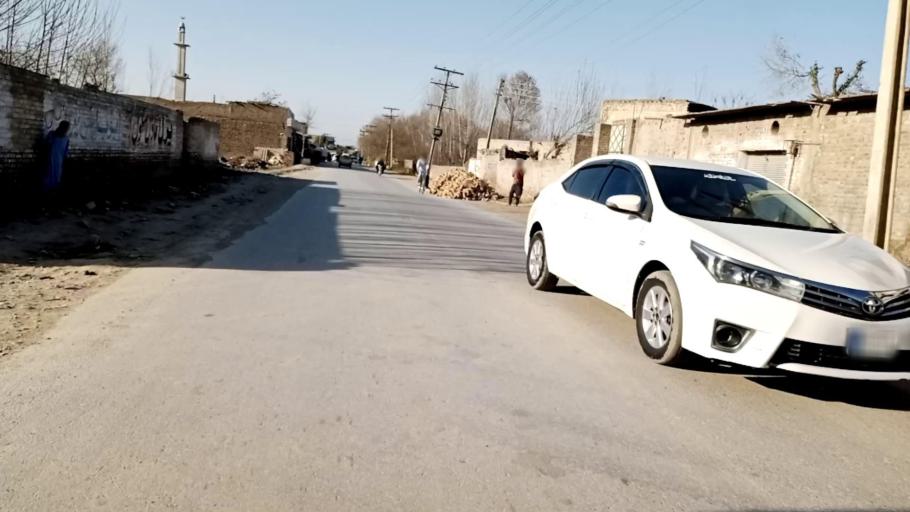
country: PK
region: Khyber Pakhtunkhwa
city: Peshawar
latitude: 34.0808
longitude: 71.5316
